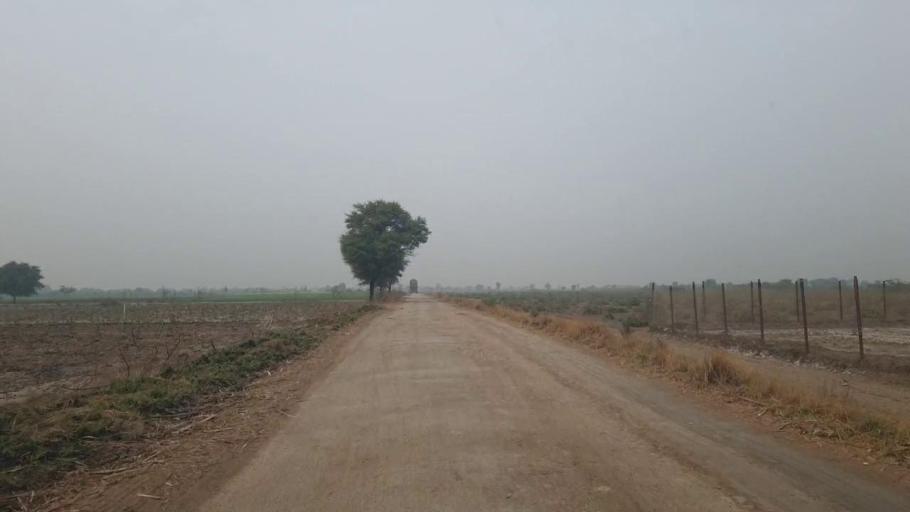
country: PK
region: Sindh
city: Tando Adam
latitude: 25.8044
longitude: 68.7213
